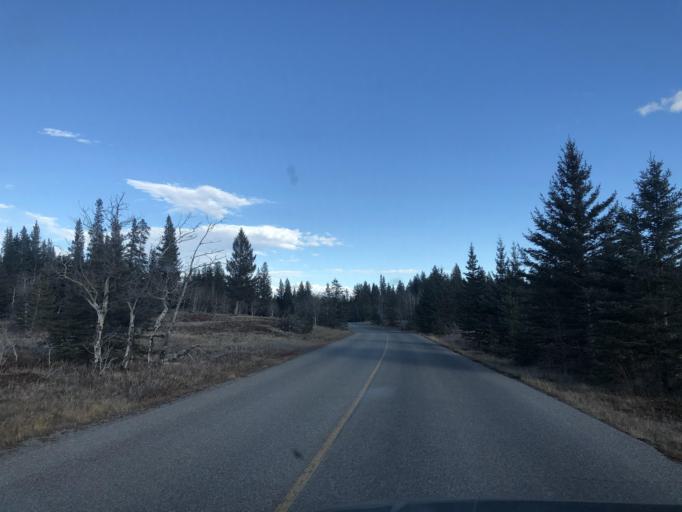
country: CA
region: Alberta
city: Canmore
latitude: 51.0796
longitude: -115.0842
